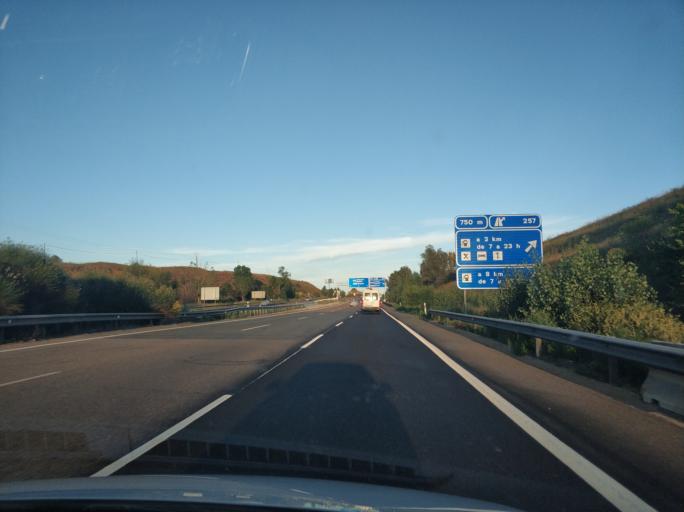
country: ES
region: Castille and Leon
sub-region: Provincia de Zamora
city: Castrogonzalo
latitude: 41.9828
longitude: -5.6222
